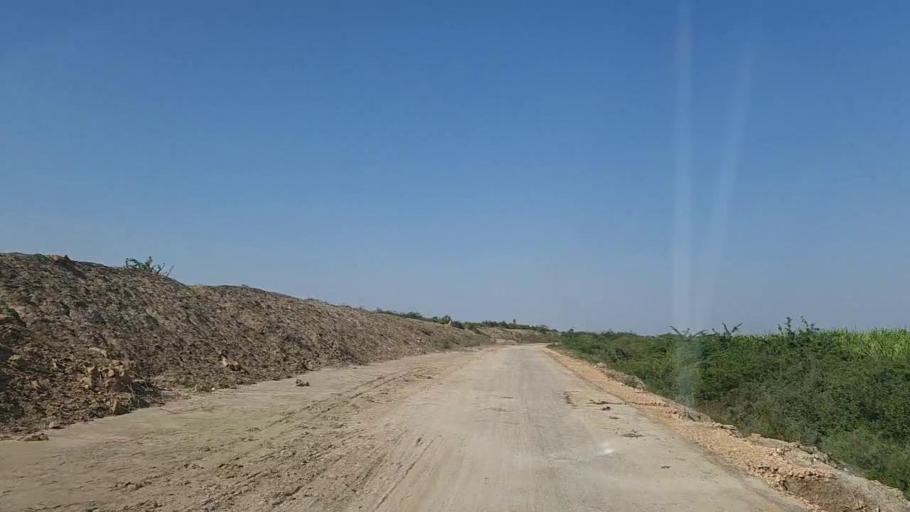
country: PK
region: Sindh
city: Chuhar Jamali
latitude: 24.5745
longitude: 68.0297
